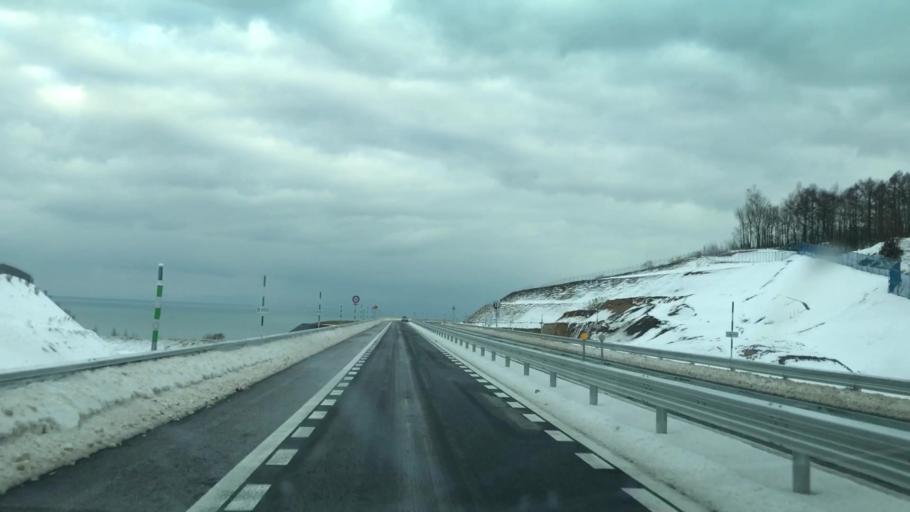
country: JP
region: Hokkaido
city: Otaru
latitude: 43.1684
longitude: 141.0650
